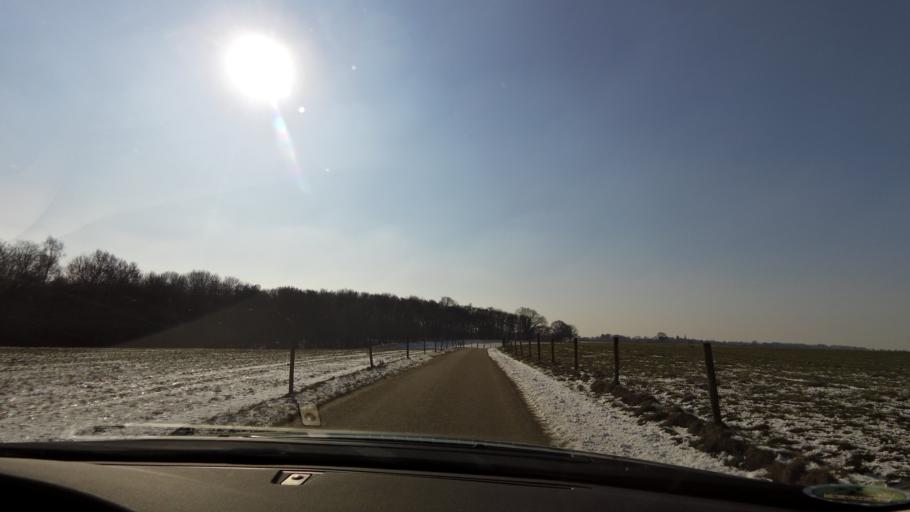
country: NL
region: Limburg
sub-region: Valkenburg aan de Geul
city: Schin op Geul
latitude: 50.8303
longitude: 5.8694
